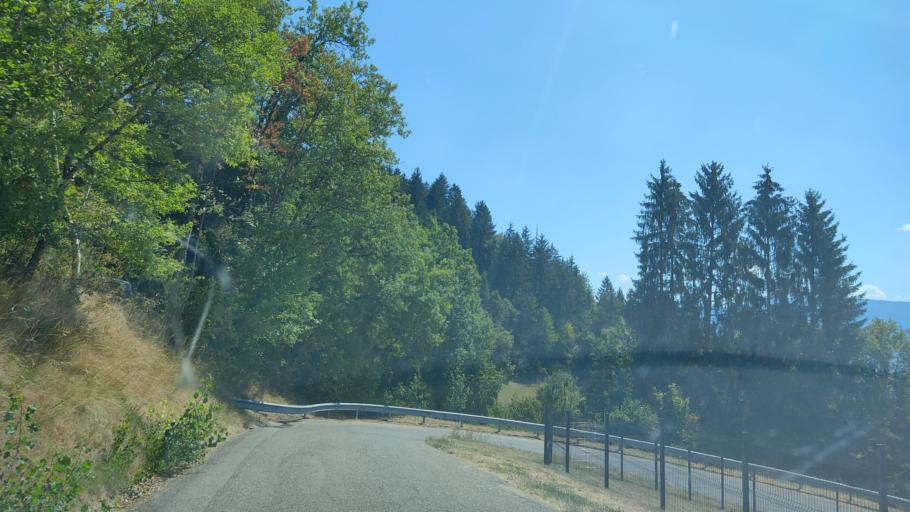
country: FR
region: Rhone-Alpes
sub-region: Departement de la Savoie
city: Novalaise
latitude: 45.6059
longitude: 5.7853
